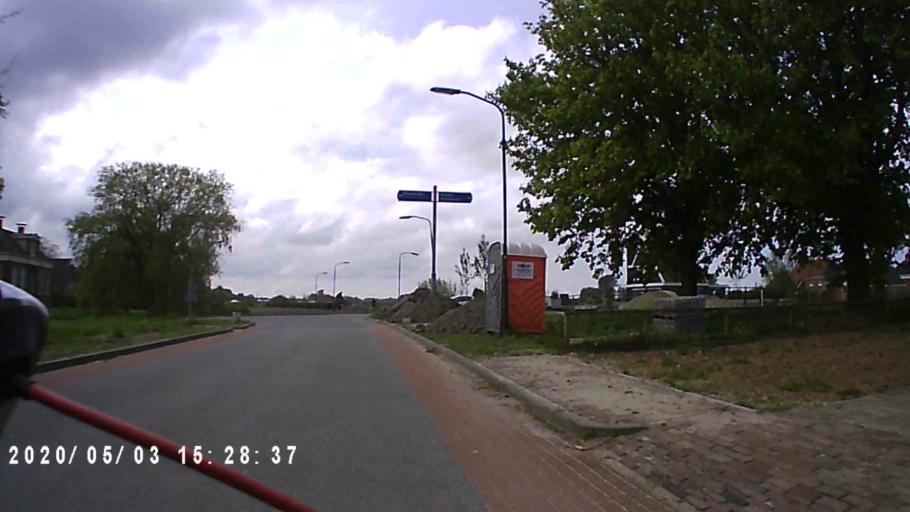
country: NL
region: Groningen
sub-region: Gemeente Winsum
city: Winsum
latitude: 53.3511
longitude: 6.4648
